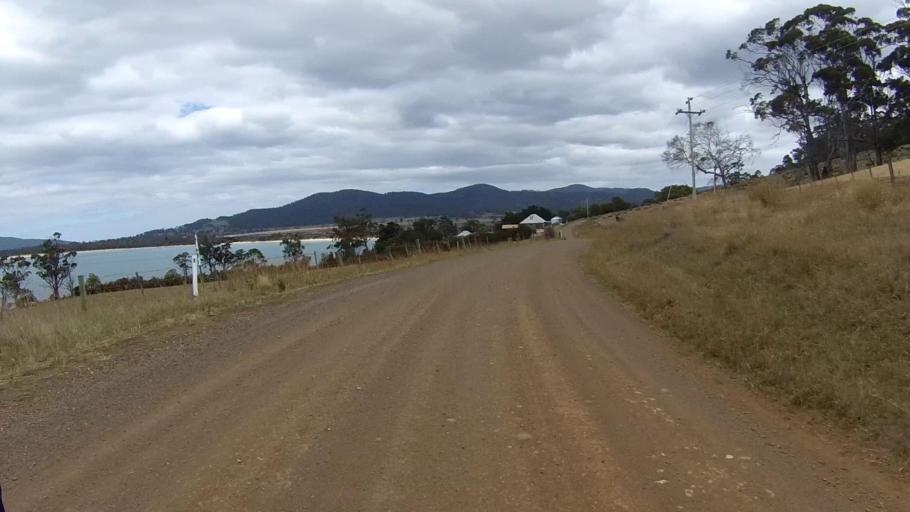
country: AU
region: Tasmania
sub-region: Sorell
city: Sorell
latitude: -42.6258
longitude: 147.9327
